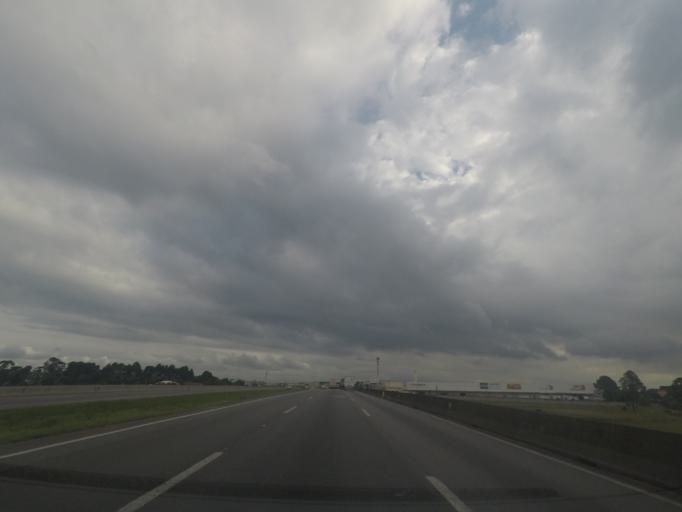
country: BR
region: Parana
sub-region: Sao Jose Dos Pinhais
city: Sao Jose dos Pinhais
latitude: -25.5348
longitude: -49.1474
